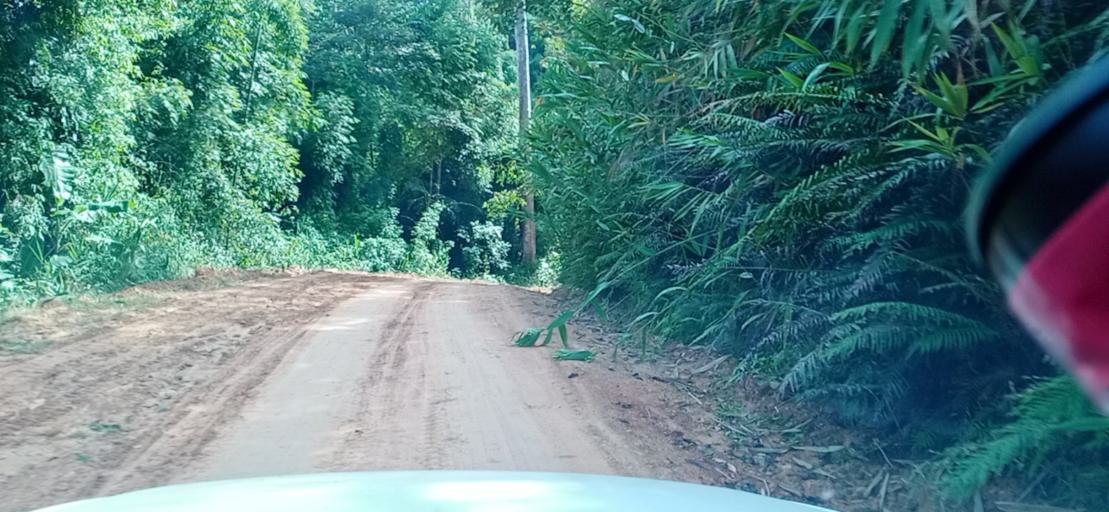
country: TH
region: Changwat Bueng Kan
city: Pak Khat
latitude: 18.6336
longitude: 103.2625
